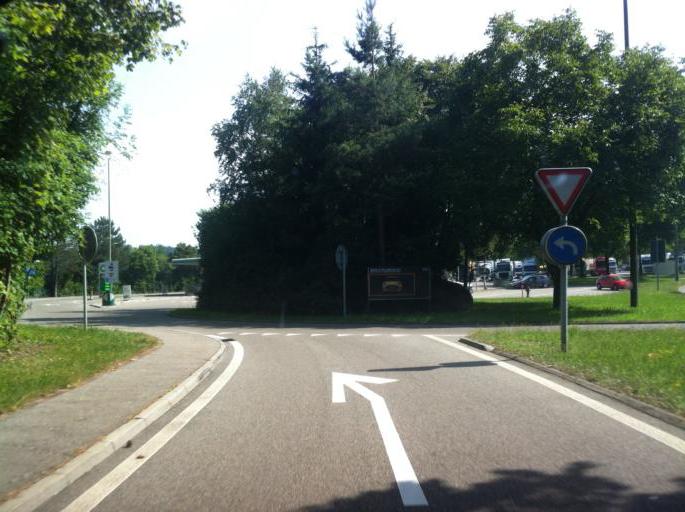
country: CH
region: Zurich
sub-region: Bezirk Pfaeffikon
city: Effretikon / Watt
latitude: 47.4510
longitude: 8.7017
